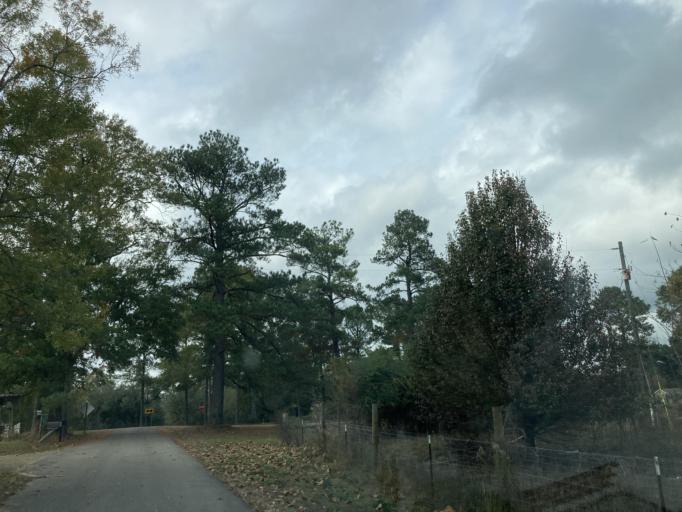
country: US
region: Mississippi
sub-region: Lamar County
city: Purvis
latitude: 31.1815
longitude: -89.5631
